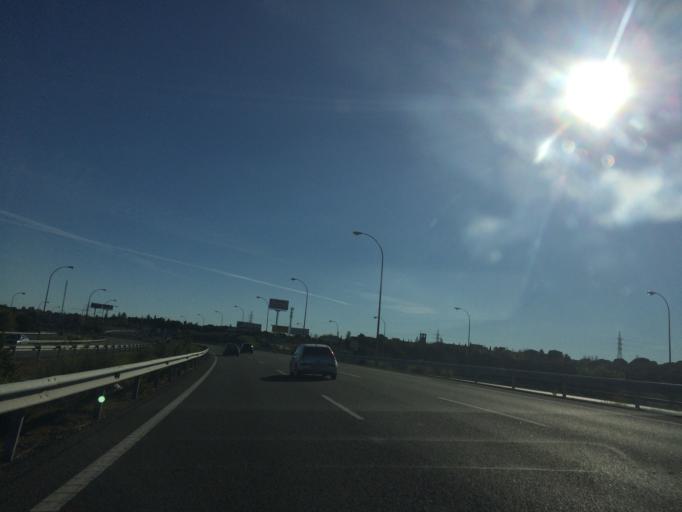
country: ES
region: Madrid
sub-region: Provincia de Madrid
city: Pozuelo de Alarcon
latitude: 40.4308
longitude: -3.8365
